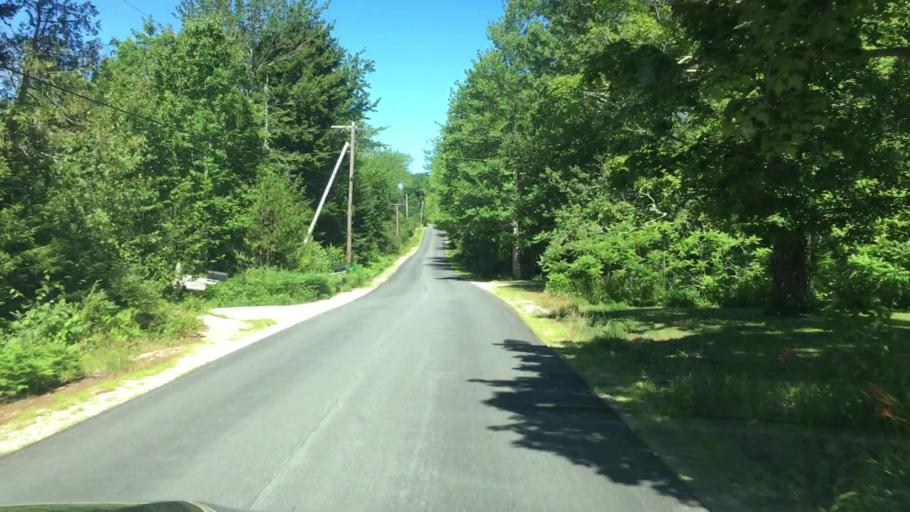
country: US
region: Maine
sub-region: Hancock County
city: Sedgwick
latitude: 44.3193
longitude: -68.6271
